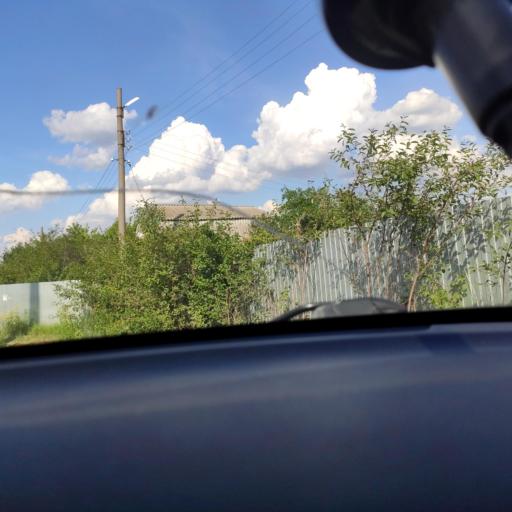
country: RU
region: Tatarstan
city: Verkhniy Uslon
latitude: 55.6476
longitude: 48.9431
